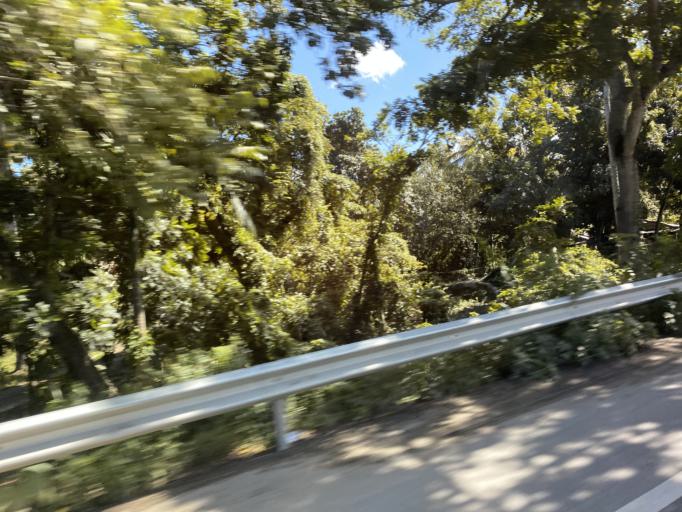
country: DO
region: Puerto Plata
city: Imbert
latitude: 19.8109
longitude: -70.7791
